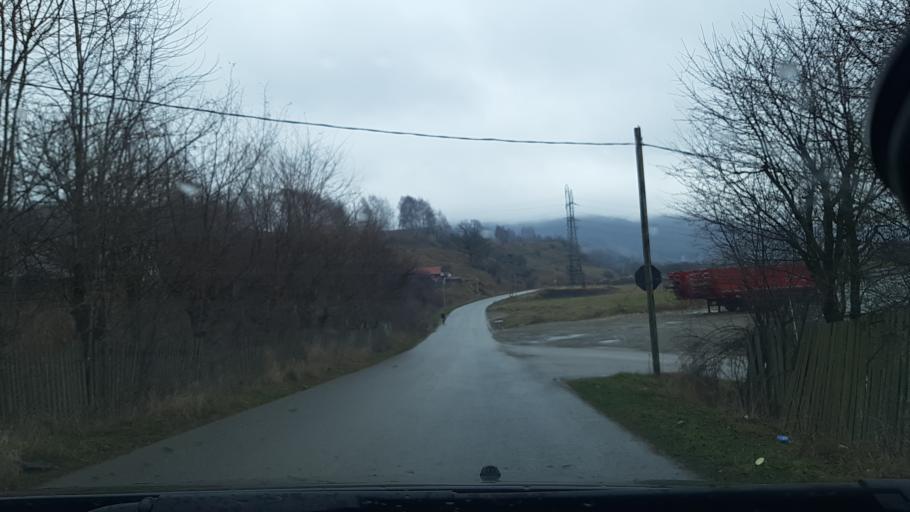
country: RO
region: Hunedoara
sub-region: Oras Petrila
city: Petrila
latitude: 45.4399
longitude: 23.4129
